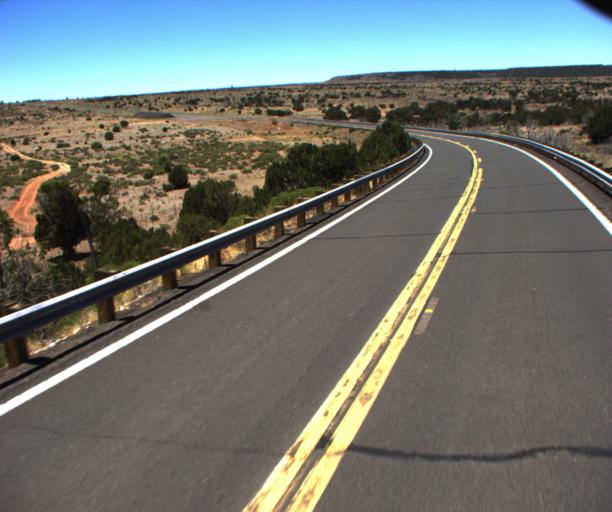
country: US
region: Arizona
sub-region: Coconino County
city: LeChee
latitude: 34.7295
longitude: -111.0772
